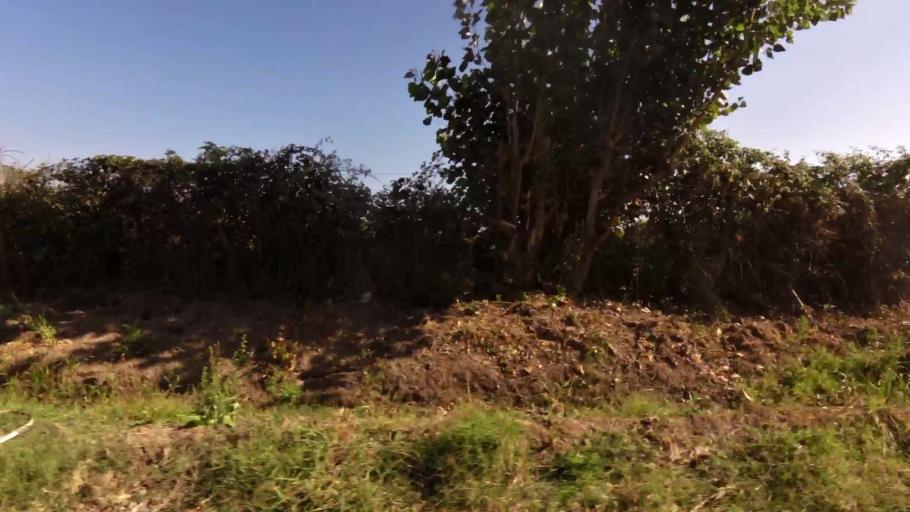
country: CL
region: Maule
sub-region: Provincia de Talca
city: Talca
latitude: -35.3997
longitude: -71.6142
